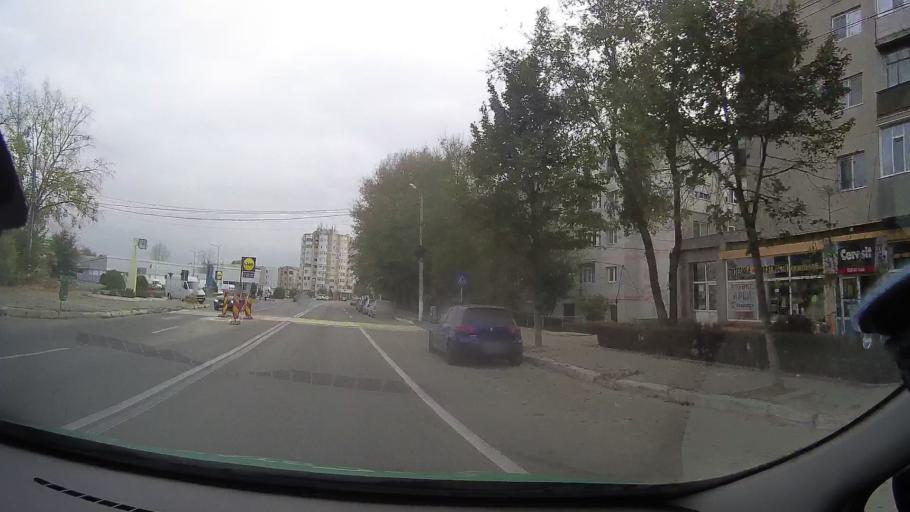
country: RO
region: Constanta
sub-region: Municipiul Medgidia
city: Medgidia
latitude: 44.2629
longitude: 28.2612
